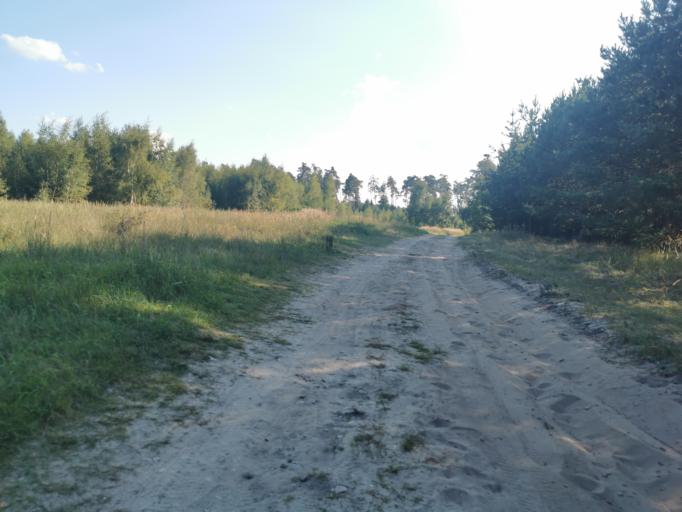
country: SK
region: Trnavsky
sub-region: Okres Senica
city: Senica
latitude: 48.6548
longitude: 17.2924
